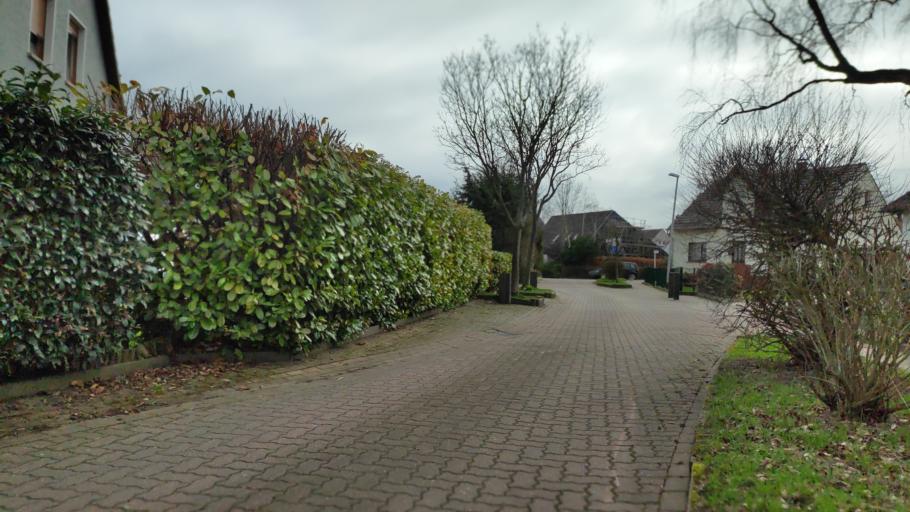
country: DE
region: North Rhine-Westphalia
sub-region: Regierungsbezirk Detmold
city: Minden
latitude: 52.2707
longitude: 8.8903
